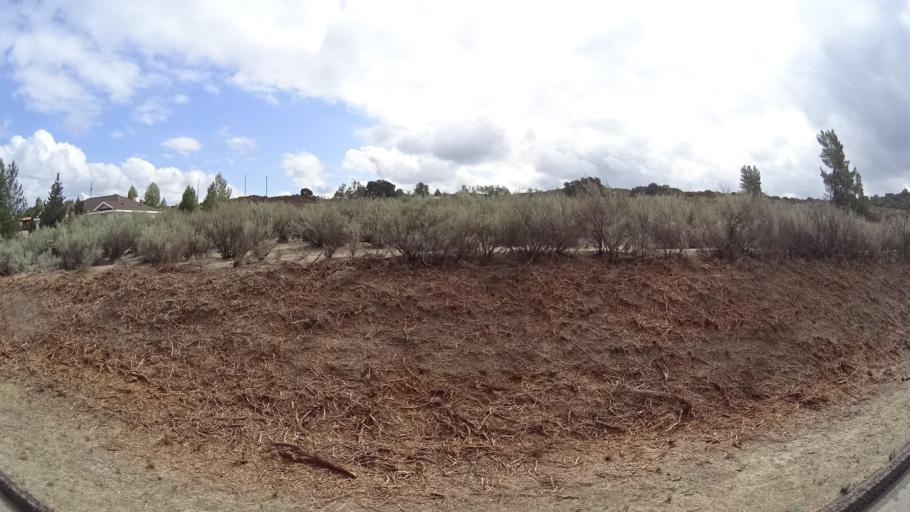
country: US
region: California
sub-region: San Diego County
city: Campo
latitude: 32.6116
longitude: -116.4699
